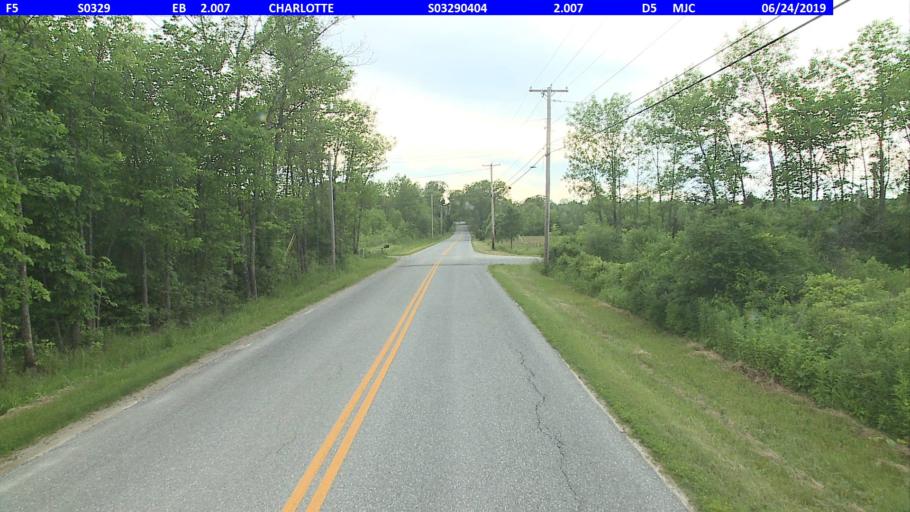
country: US
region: Vermont
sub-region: Addison County
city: Vergennes
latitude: 44.3069
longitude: -73.2858
